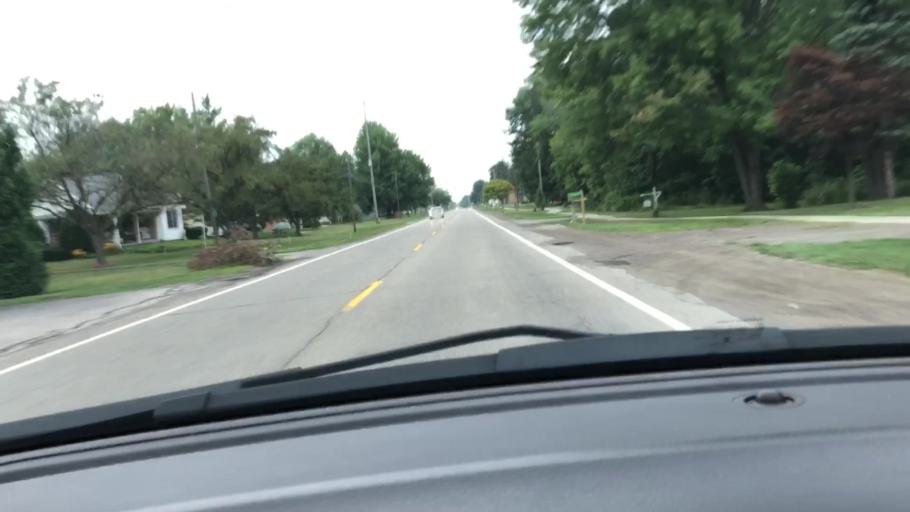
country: US
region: Michigan
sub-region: Bay County
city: Auburn
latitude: 43.6039
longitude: -84.1043
